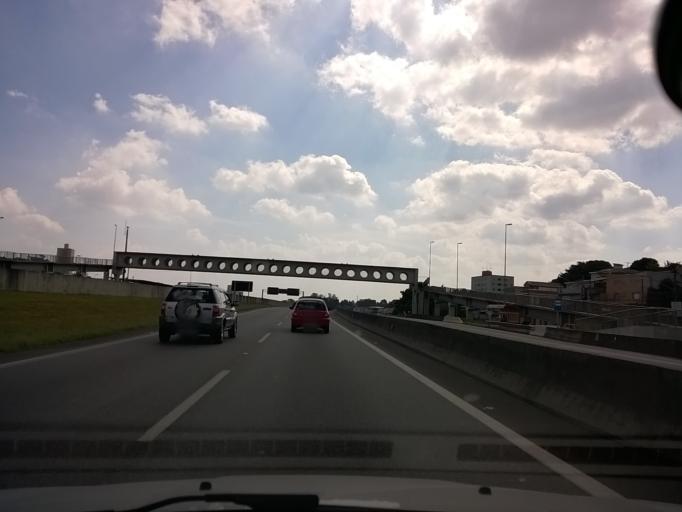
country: BR
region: Sao Paulo
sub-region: Osasco
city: Osasco
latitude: -23.5077
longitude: -46.7438
